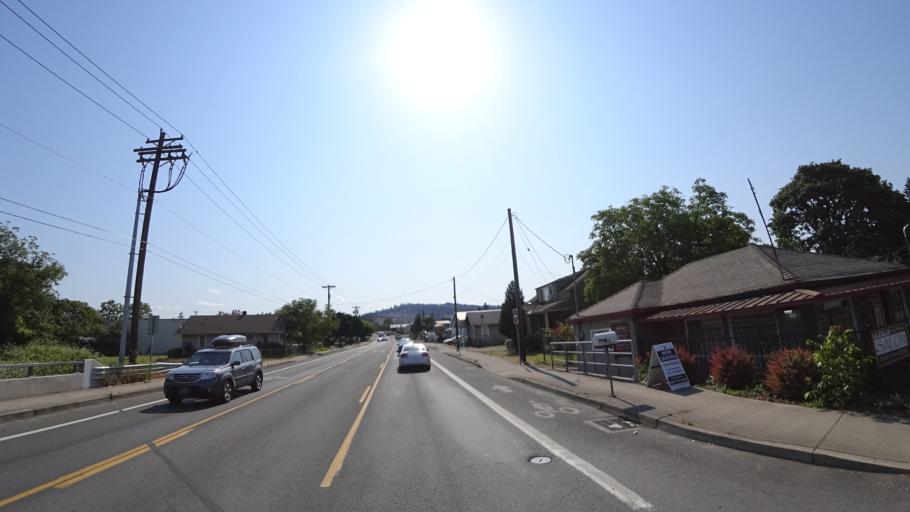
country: US
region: Oregon
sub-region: Multnomah County
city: Lents
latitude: 45.4559
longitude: -122.5906
